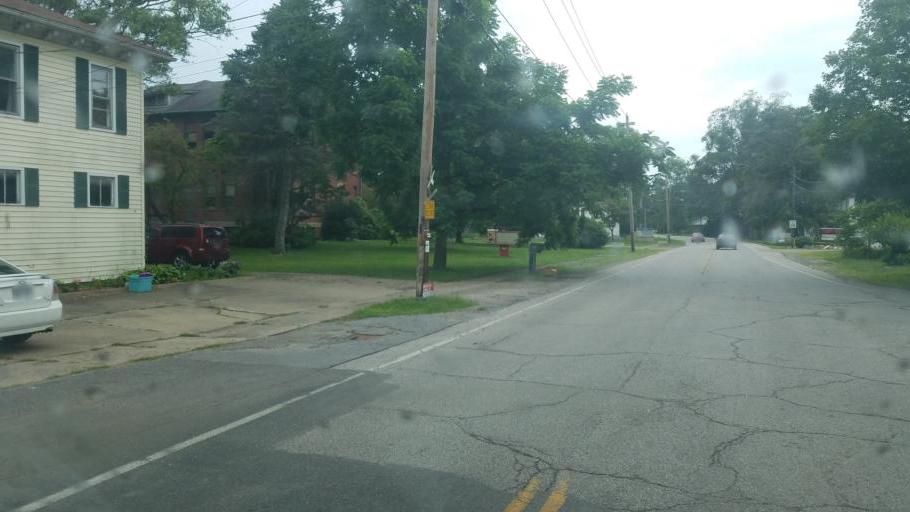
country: US
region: Ohio
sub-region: Summit County
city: Clinton
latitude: 40.9267
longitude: -81.6274
